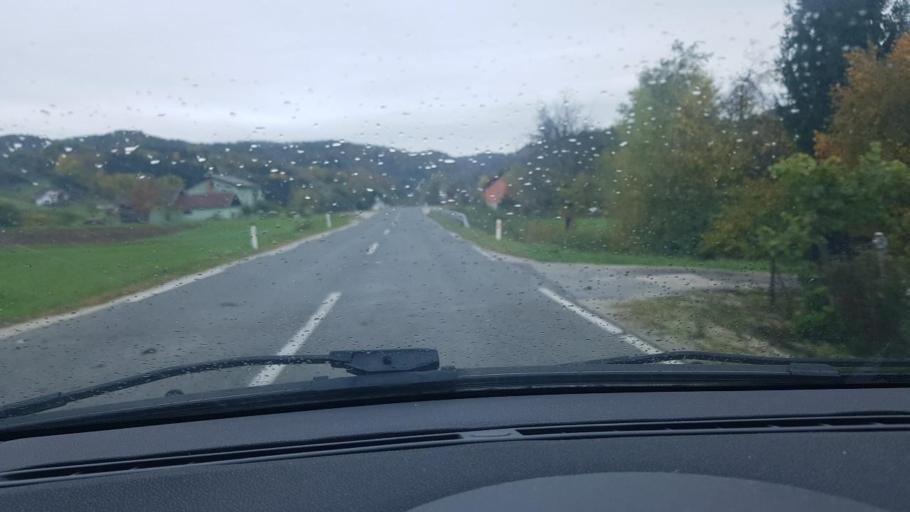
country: SI
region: Rogatec
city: Rogatec
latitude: 46.2446
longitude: 15.7010
